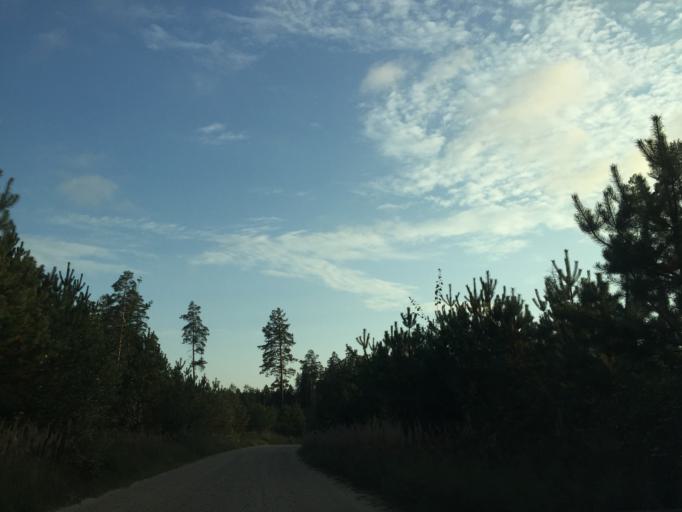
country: LV
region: Baldone
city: Baldone
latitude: 56.7579
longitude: 24.4091
